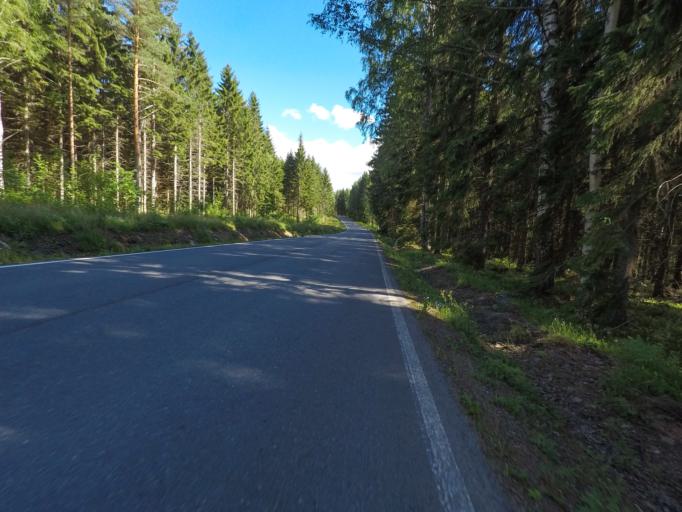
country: FI
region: South Karelia
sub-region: Lappeenranta
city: Taipalsaari
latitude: 61.1750
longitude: 28.0145
